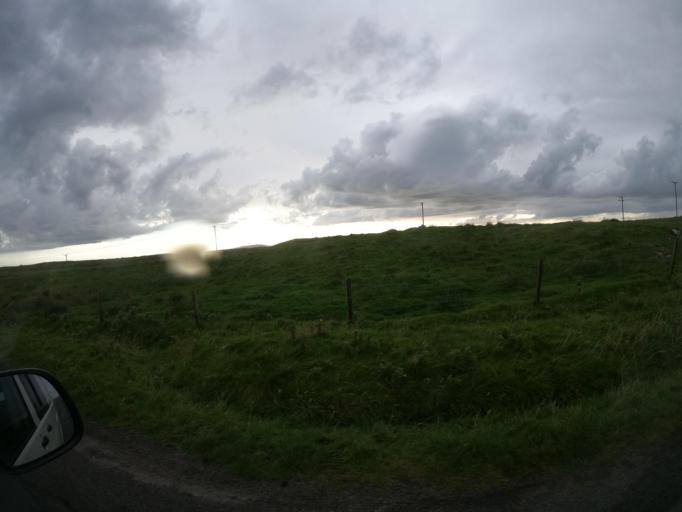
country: GB
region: Scotland
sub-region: Eilean Siar
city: Barra
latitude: 56.5088
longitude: -6.8107
